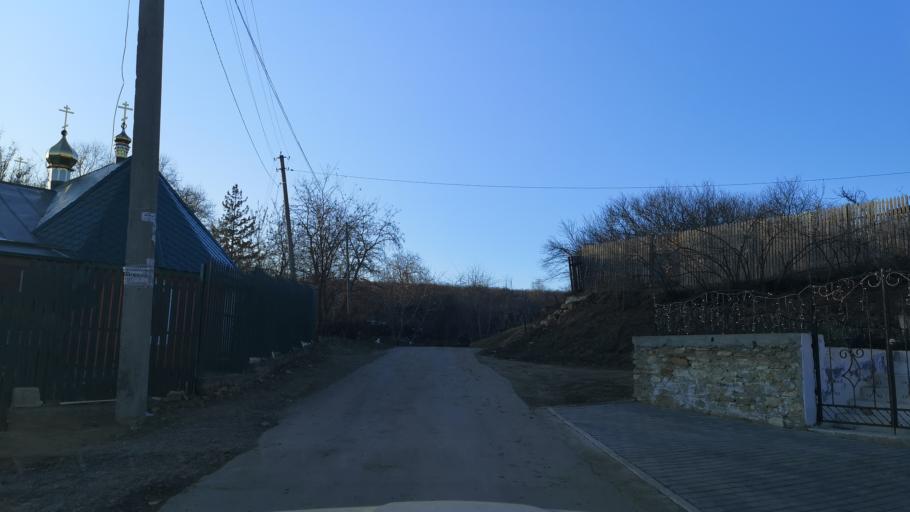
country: MD
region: Orhei
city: Orhei
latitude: 47.3682
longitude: 28.6913
